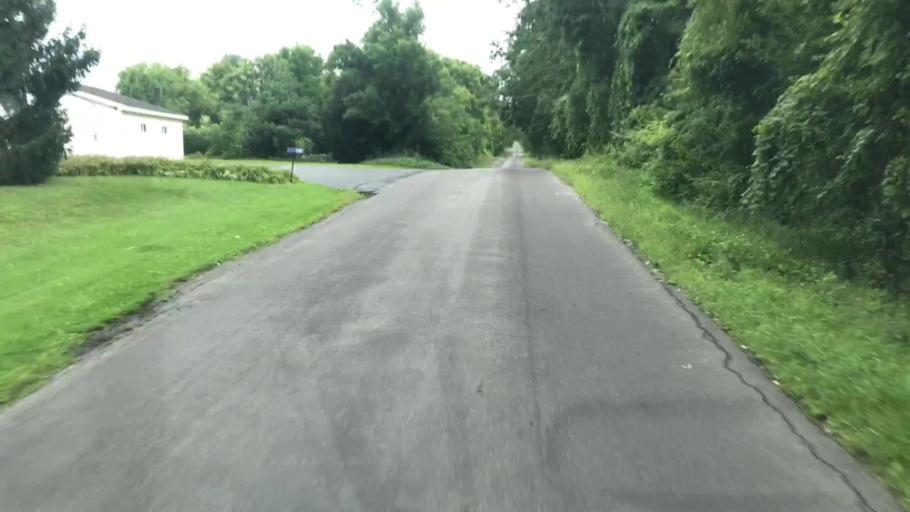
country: US
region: New York
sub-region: Onondaga County
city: Elbridge
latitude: 43.0047
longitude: -76.4508
